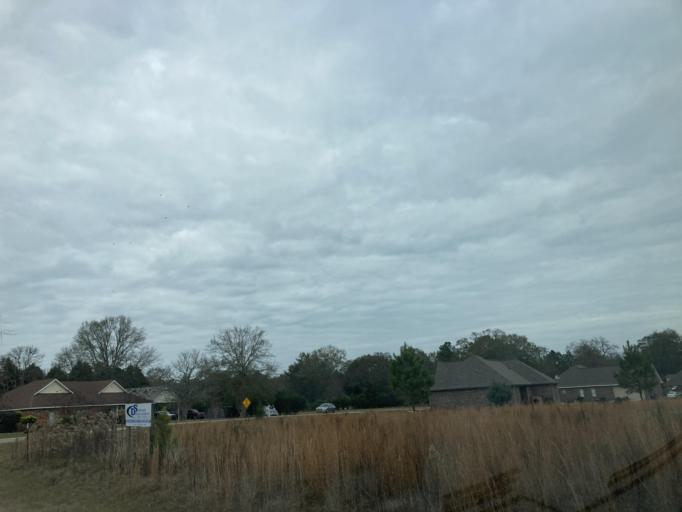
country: US
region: Mississippi
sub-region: Lamar County
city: Purvis
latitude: 31.1448
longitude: -89.2625
